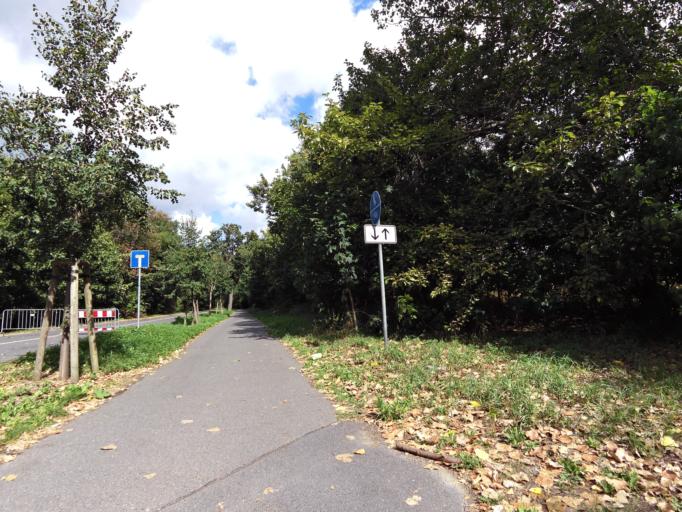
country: DE
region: Brandenburg
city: Grossbeeren
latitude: 52.3861
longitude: 13.3322
